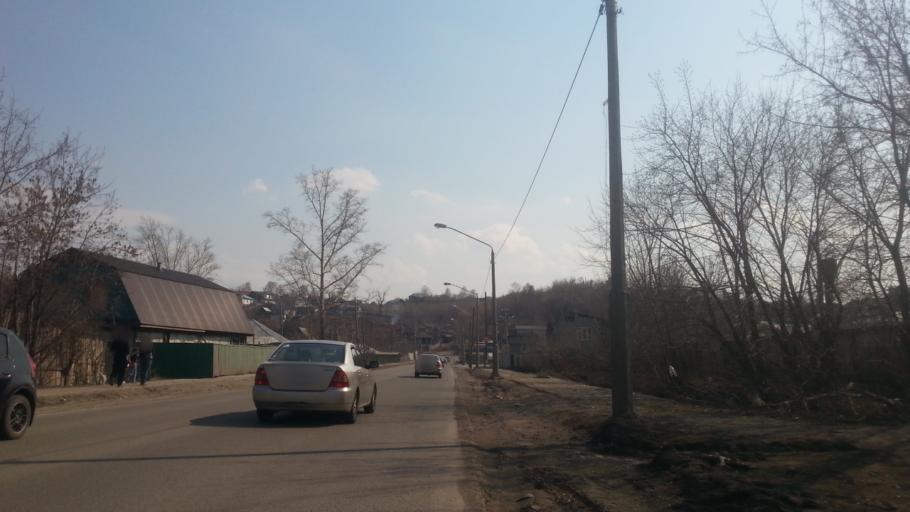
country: RU
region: Altai Krai
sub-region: Gorod Barnaulskiy
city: Barnaul
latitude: 53.3212
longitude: 83.7694
